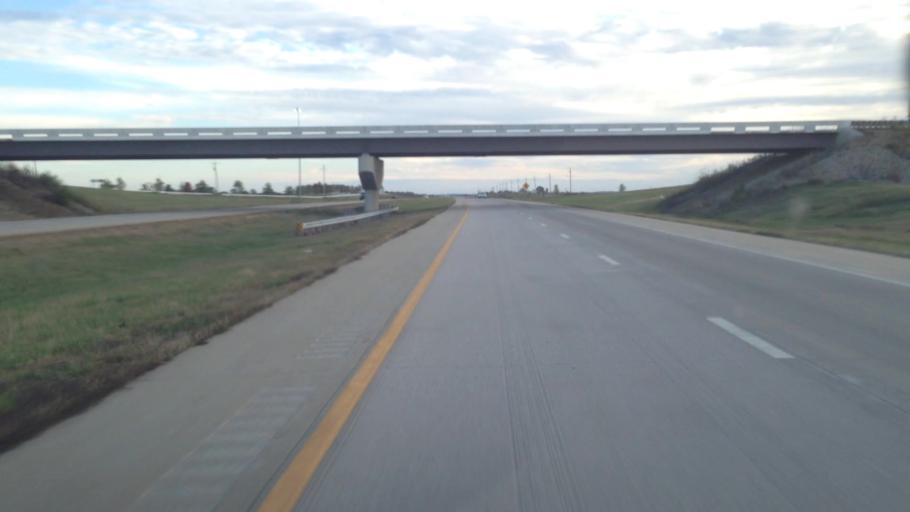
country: US
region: Kansas
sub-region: Douglas County
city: Baldwin City
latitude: 38.8341
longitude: -95.2691
